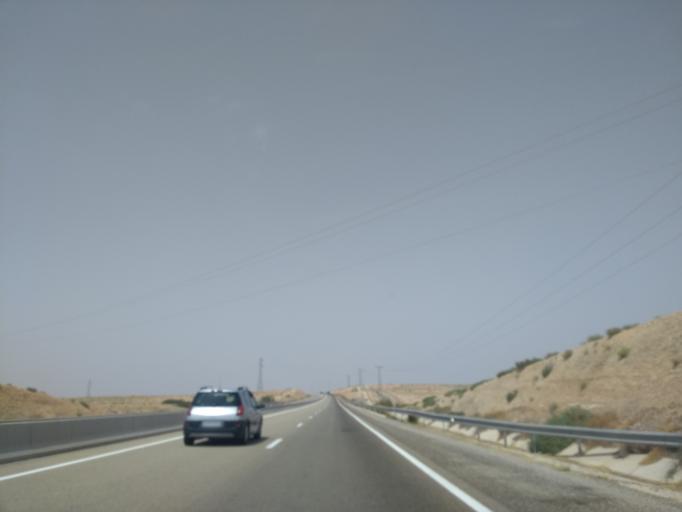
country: MA
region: Marrakech-Tensift-Al Haouz
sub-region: Chichaoua
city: Chichaoua
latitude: 31.4193
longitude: -8.7386
